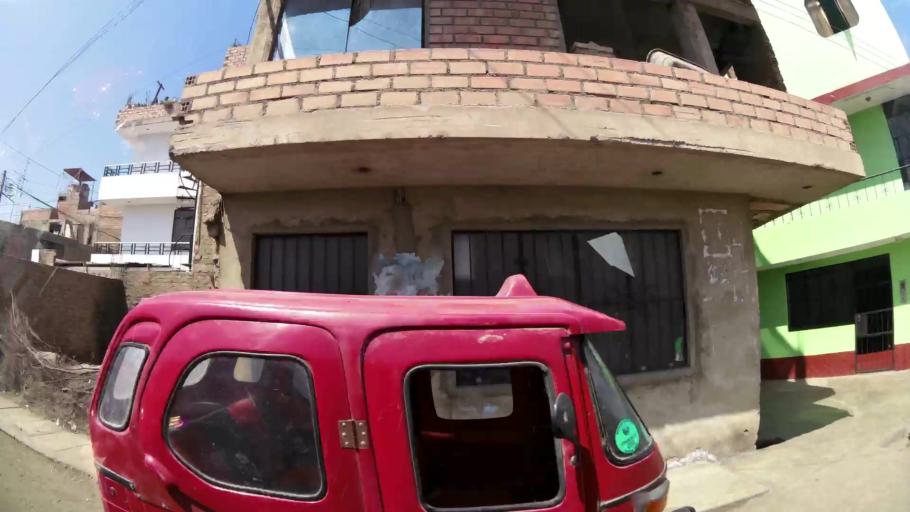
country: PE
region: Lima
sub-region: Provincia de Canete
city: Mala
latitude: -12.6538
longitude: -76.6362
